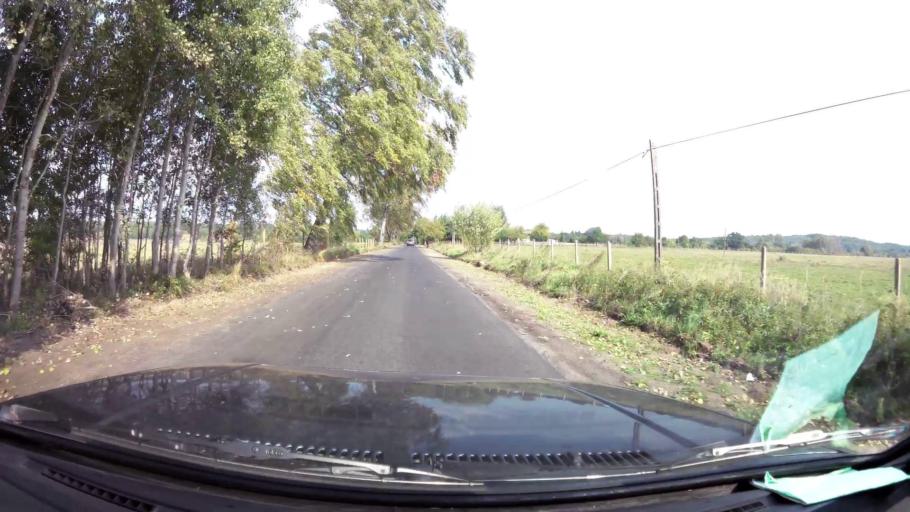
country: PL
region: West Pomeranian Voivodeship
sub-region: Powiat koszalinski
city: Bobolice
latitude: 54.1095
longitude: 16.5007
